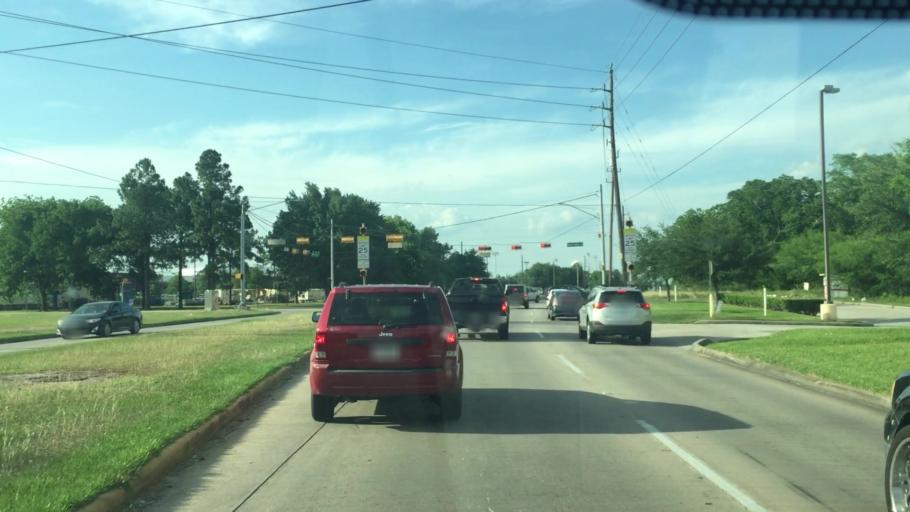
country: US
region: Texas
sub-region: Harris County
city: Hudson
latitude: 29.9621
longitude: -95.4985
